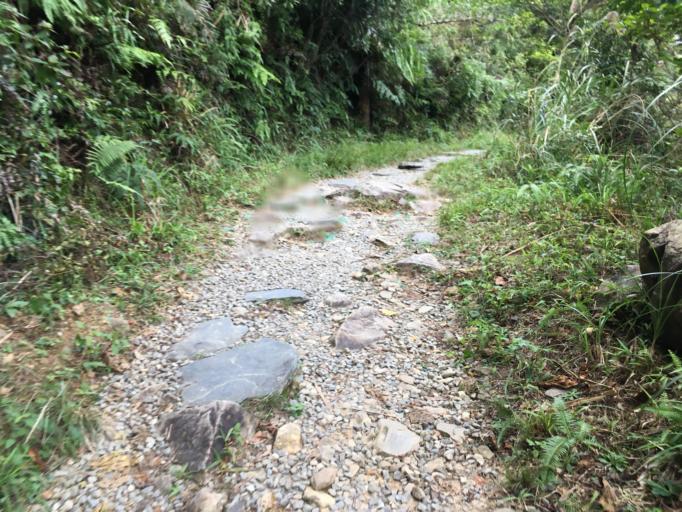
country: TW
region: Taiwan
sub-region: Yilan
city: Yilan
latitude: 24.8474
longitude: 121.7753
